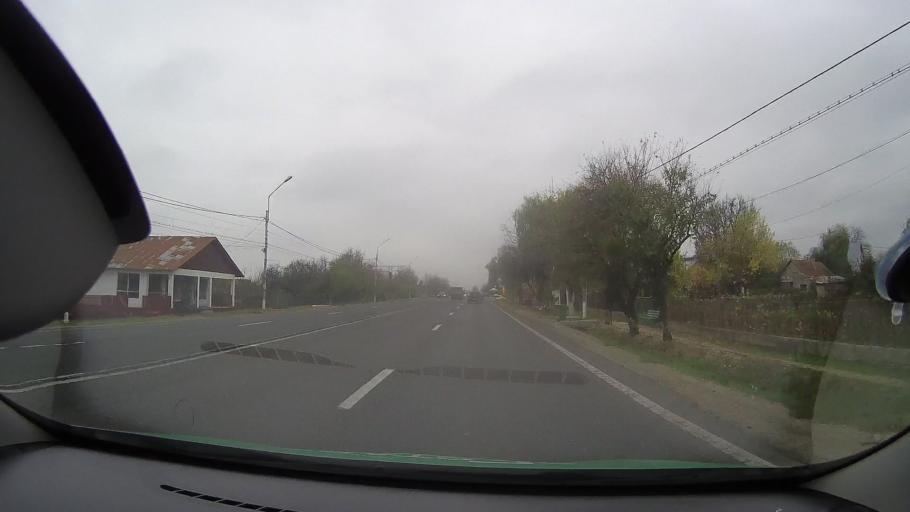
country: RO
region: Ilfov
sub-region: Comuna Ciolpani
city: Ciolpani
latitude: 44.6832
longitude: 26.0779
